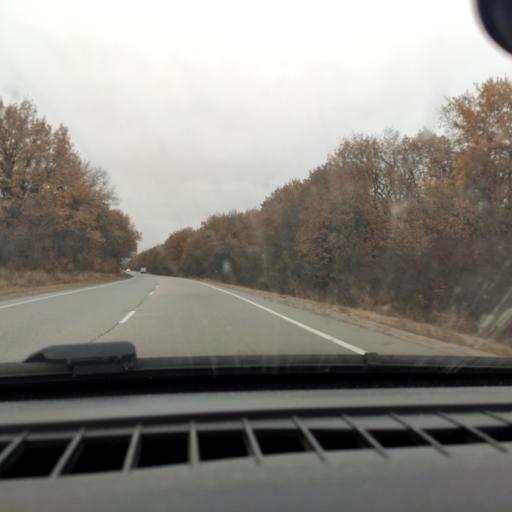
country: RU
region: Voronezj
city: Devitsa
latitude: 51.6115
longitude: 38.9807
